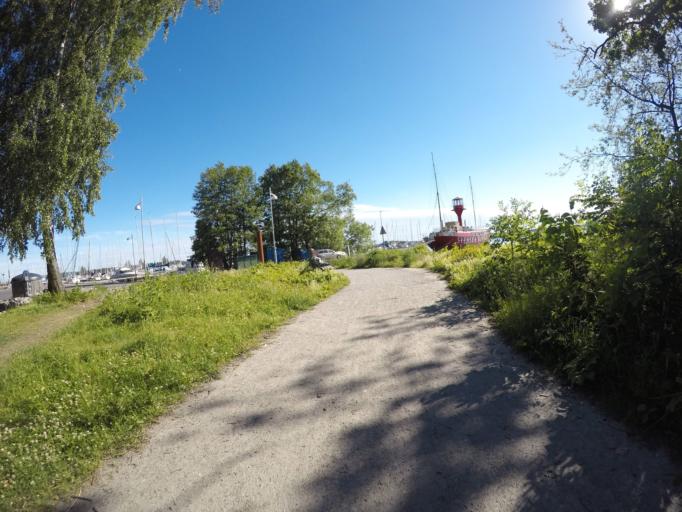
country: SE
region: Vaestmanland
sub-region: Vasteras
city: Vasteras
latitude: 59.6021
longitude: 16.5735
